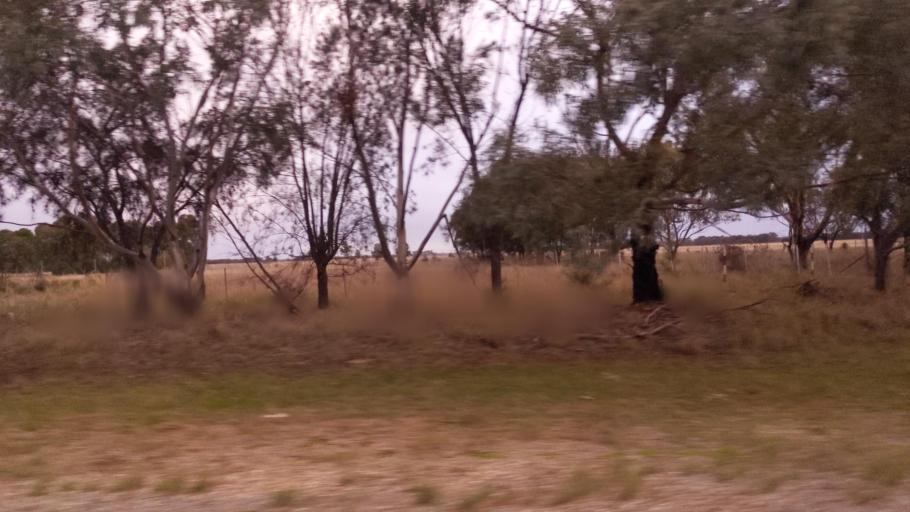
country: AU
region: New South Wales
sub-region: Coolamon
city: Coolamon
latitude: -34.7669
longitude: 146.9155
